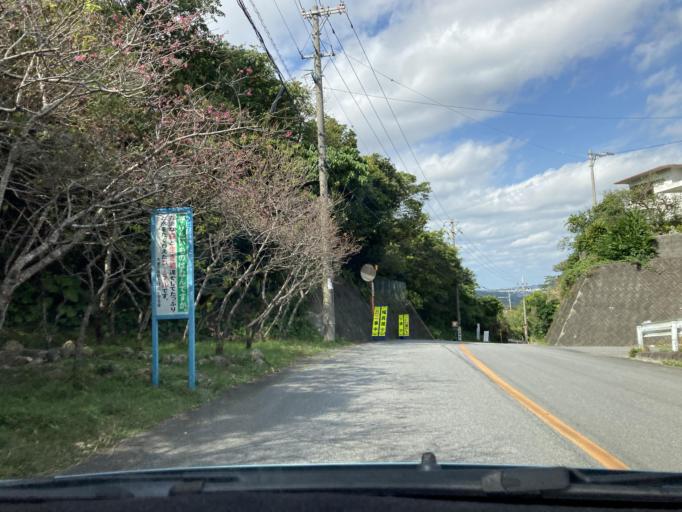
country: JP
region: Okinawa
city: Tomigusuku
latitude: 26.1836
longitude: 127.7589
